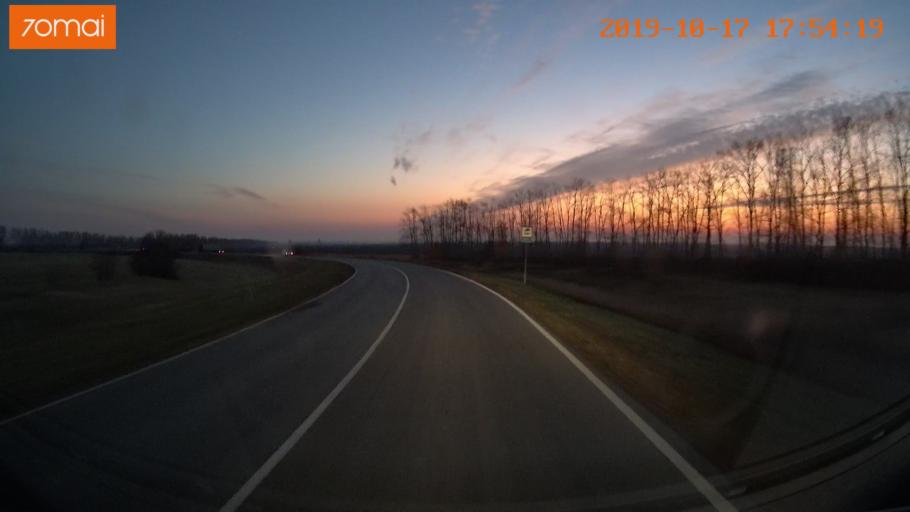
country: RU
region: Tula
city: Kurkino
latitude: 53.6089
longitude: 38.6674
